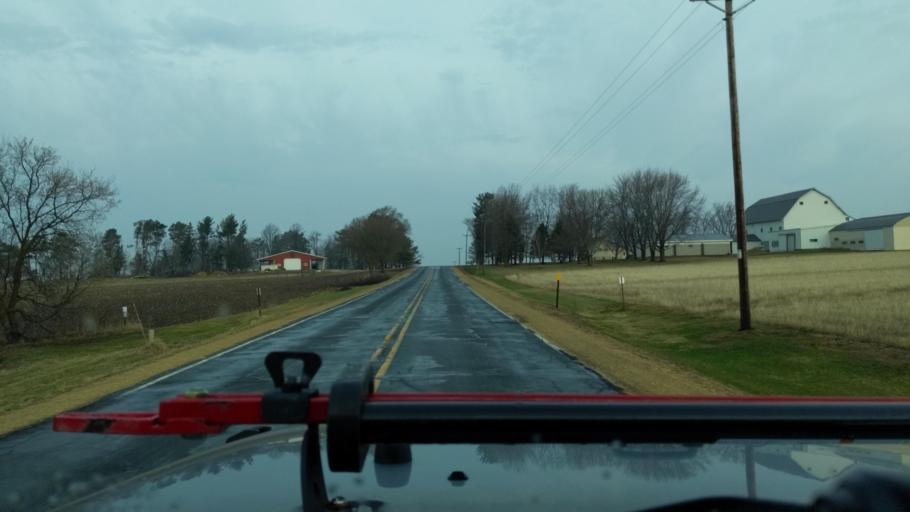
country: US
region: Wisconsin
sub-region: Saint Croix County
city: Hammond
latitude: 44.9200
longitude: -92.4399
